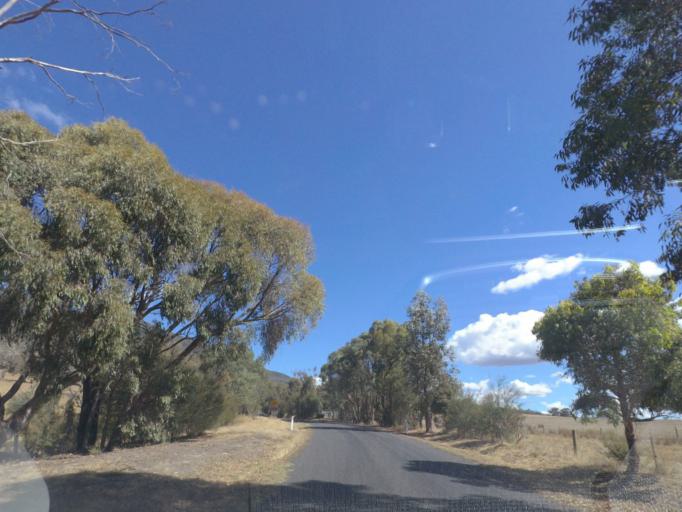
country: AU
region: Victoria
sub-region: Murrindindi
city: Alexandra
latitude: -37.2998
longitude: 145.8304
